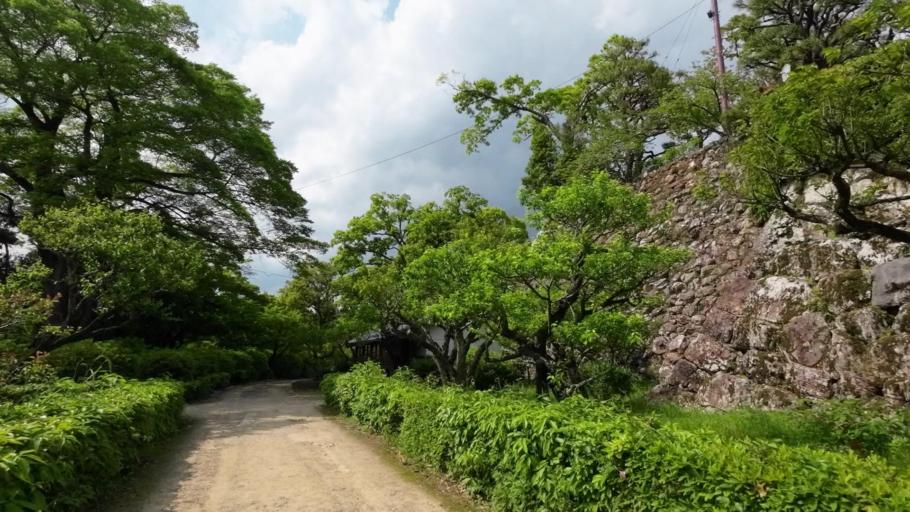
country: JP
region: Kochi
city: Kochi-shi
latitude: 33.5613
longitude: 133.5304
